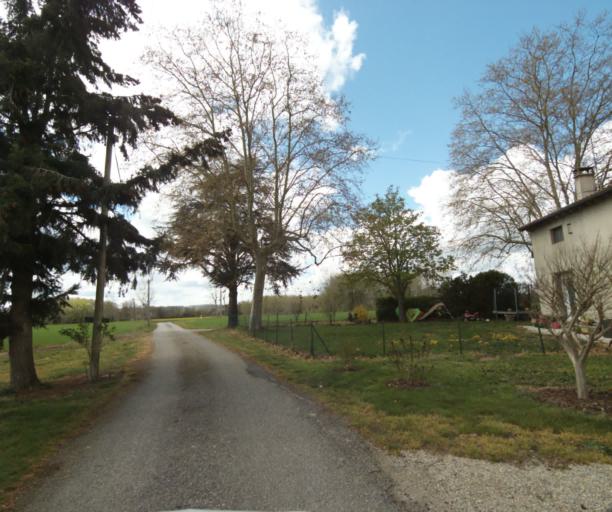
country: FR
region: Midi-Pyrenees
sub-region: Departement de l'Ariege
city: Saverdun
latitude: 43.2649
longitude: 1.5858
